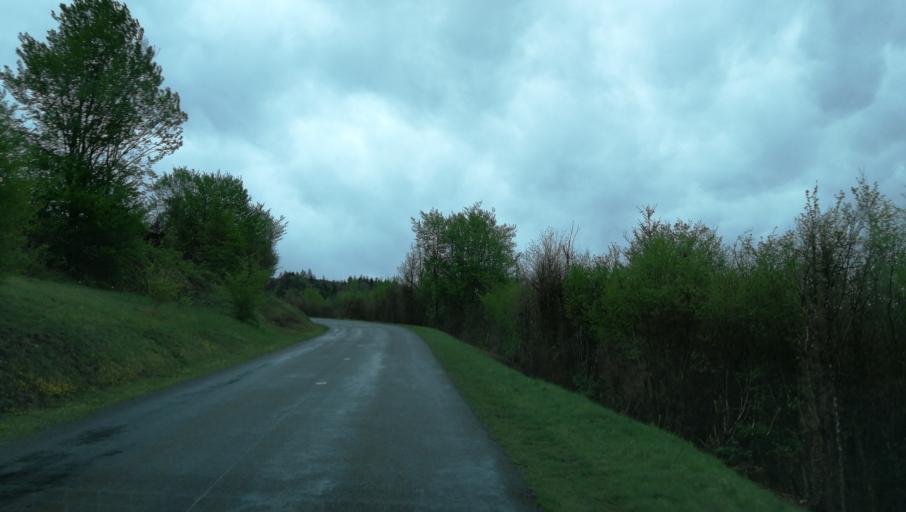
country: FR
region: Franche-Comte
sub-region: Departement du Jura
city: Moirans-en-Montagne
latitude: 46.4654
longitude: 5.6979
